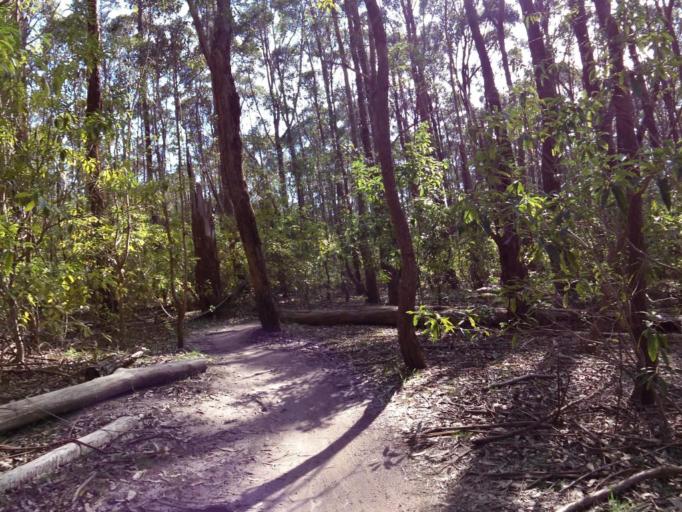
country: AU
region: Victoria
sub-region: Yarra Ranges
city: Lysterfield
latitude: -37.9395
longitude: 145.2923
